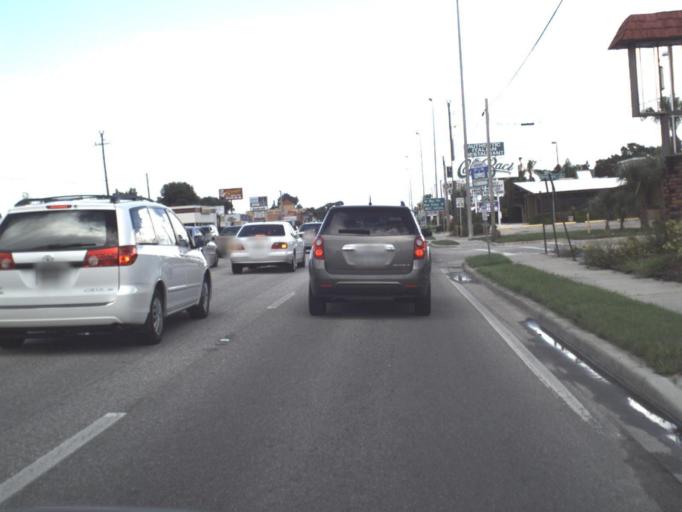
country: US
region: Florida
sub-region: Sarasota County
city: South Sarasota
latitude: 27.2961
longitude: -82.5305
